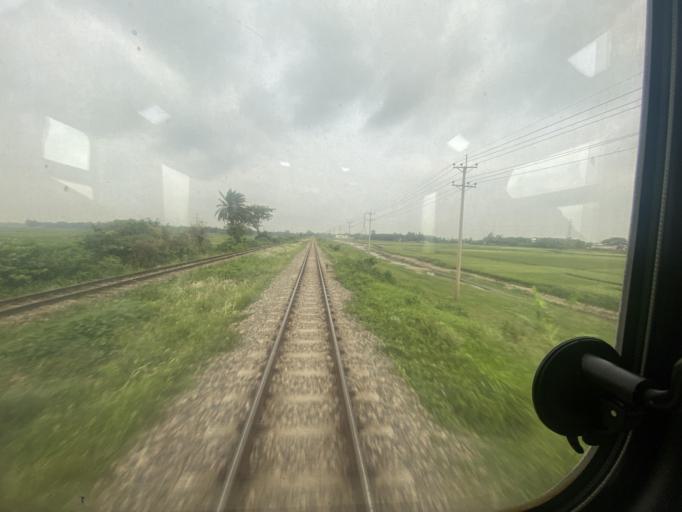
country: BD
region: Dhaka
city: Tungi
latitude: 23.9330
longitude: 90.5060
